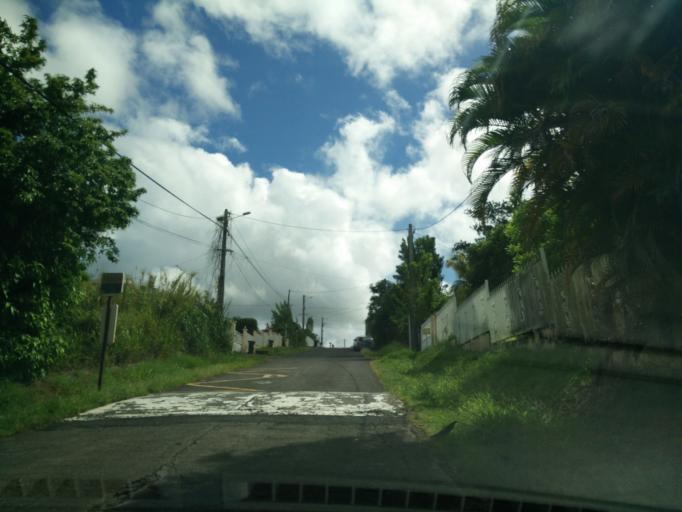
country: MQ
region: Martinique
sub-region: Martinique
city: Le Lamentin
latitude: 14.6227
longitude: -61.0158
